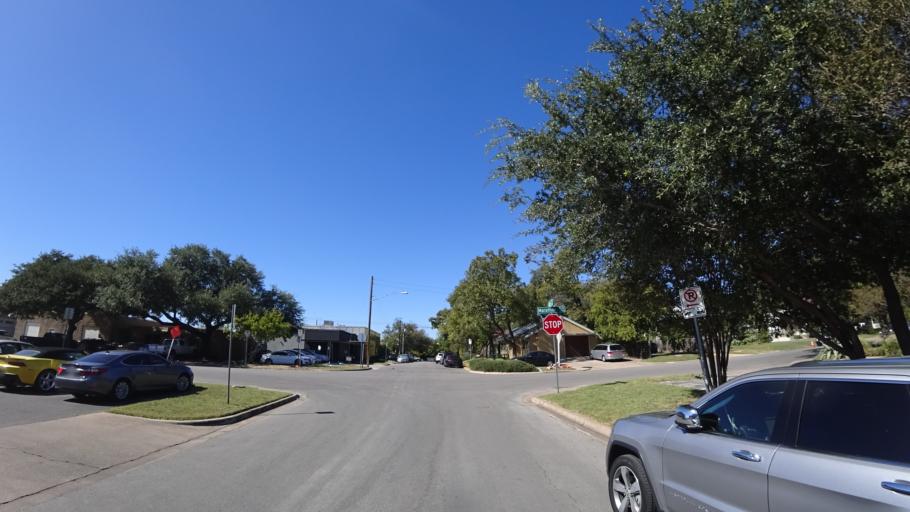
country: US
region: Texas
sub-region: Travis County
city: Austin
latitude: 30.3093
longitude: -97.7415
